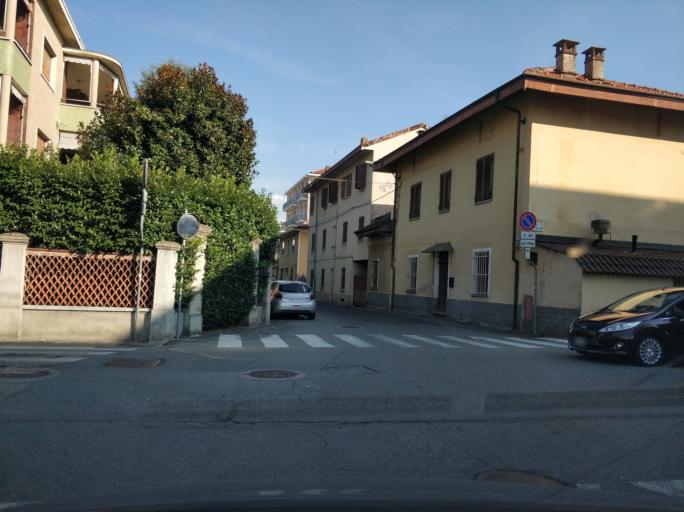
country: IT
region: Piedmont
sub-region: Provincia di Torino
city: San Maurizio
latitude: 45.2160
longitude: 7.6326
